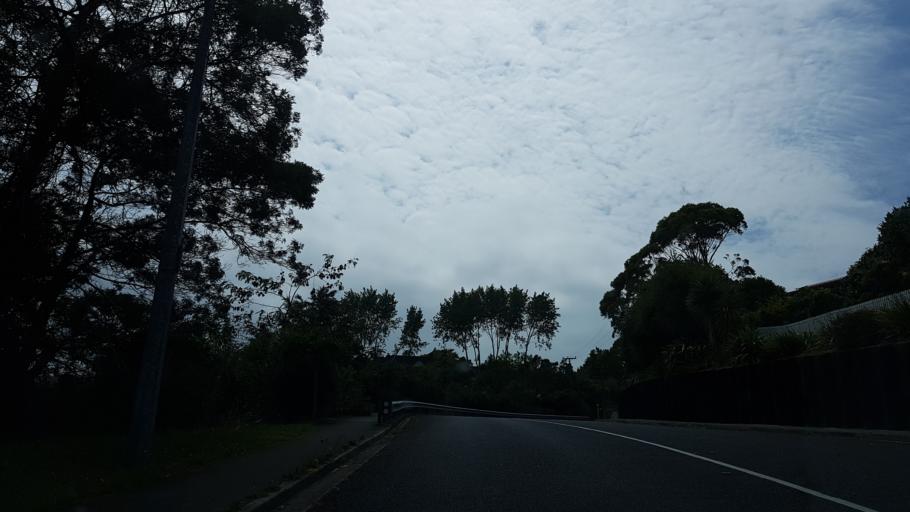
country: NZ
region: Auckland
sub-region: Auckland
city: North Shore
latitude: -36.7688
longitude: 174.7117
